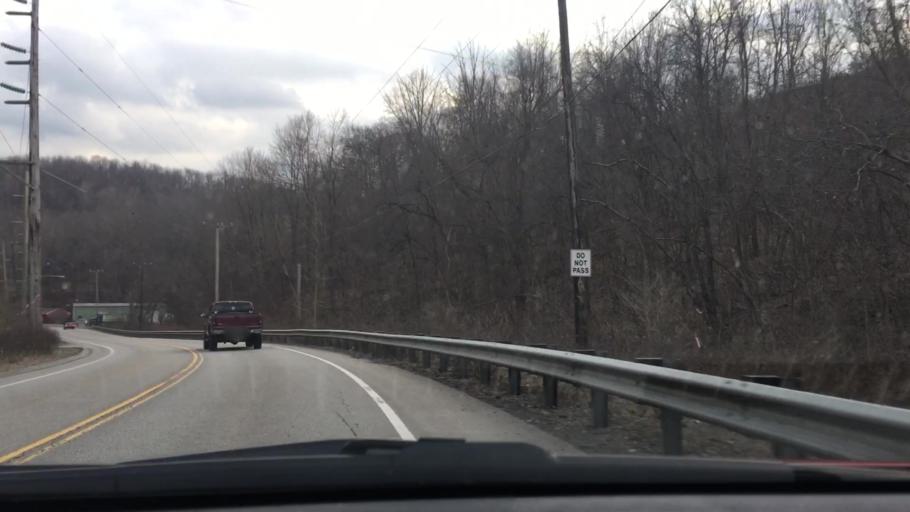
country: US
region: Pennsylvania
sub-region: Allegheny County
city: Glassport
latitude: 40.3259
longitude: -79.9109
